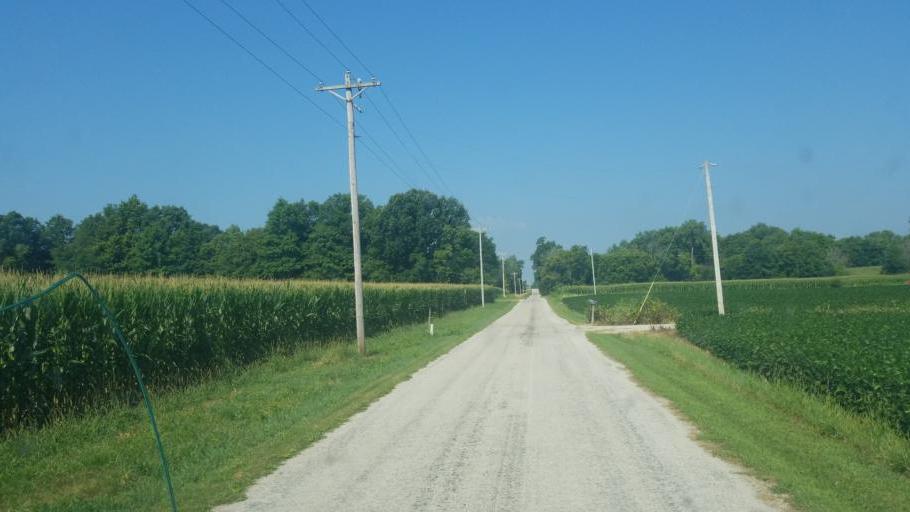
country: US
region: Ohio
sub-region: Wyandot County
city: Upper Sandusky
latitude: 40.6582
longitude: -83.3699
